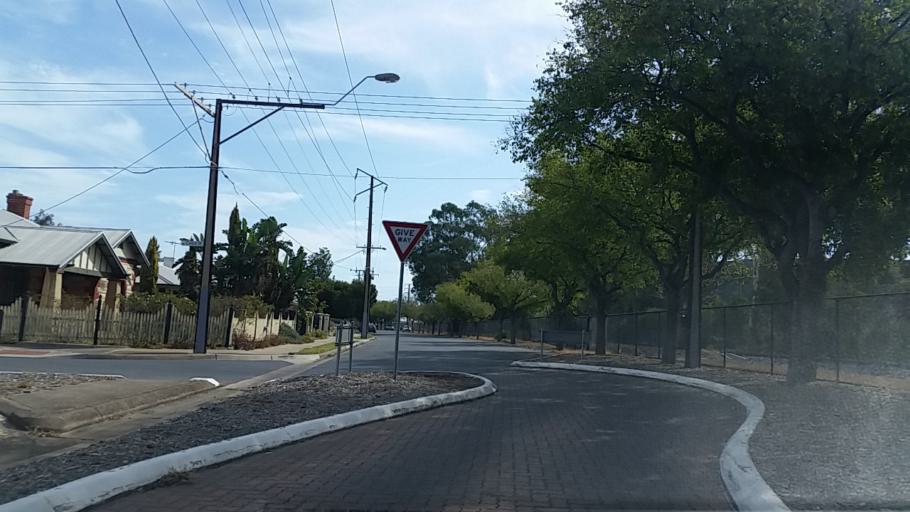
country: AU
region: South Australia
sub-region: Charles Sturt
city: Woodville West
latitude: -34.8762
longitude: 138.5324
